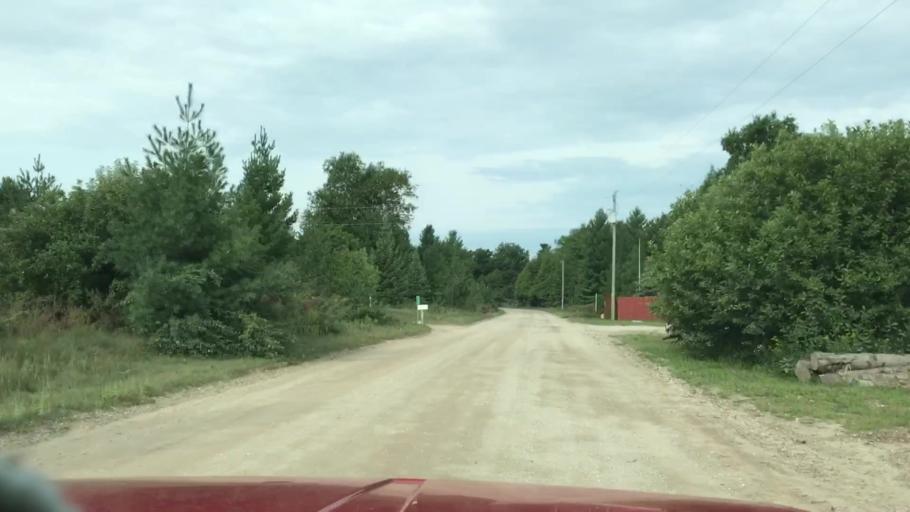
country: US
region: Michigan
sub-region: Charlevoix County
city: Charlevoix
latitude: 45.7286
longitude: -85.5275
